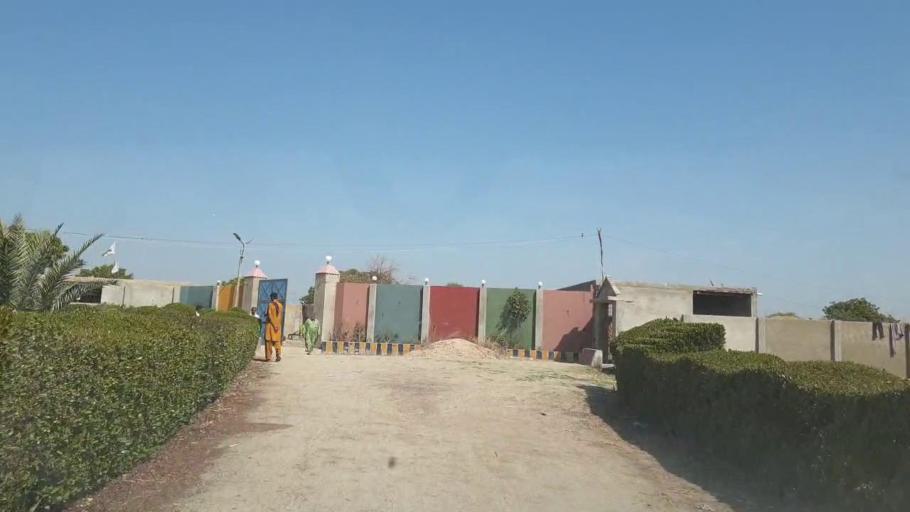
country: PK
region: Sindh
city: Mirpur Khas
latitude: 25.6624
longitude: 69.1089
